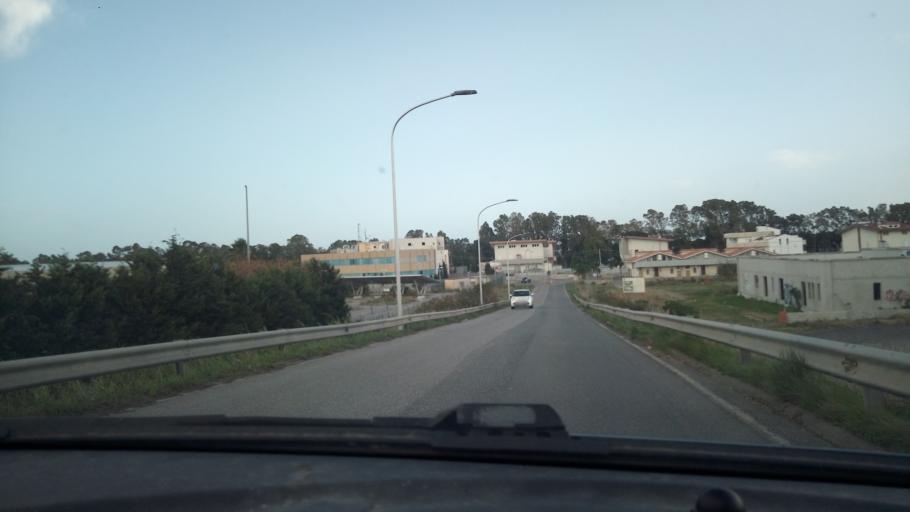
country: IT
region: Calabria
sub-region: Provincia di Catanzaro
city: Barone
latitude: 38.8329
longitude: 16.6384
